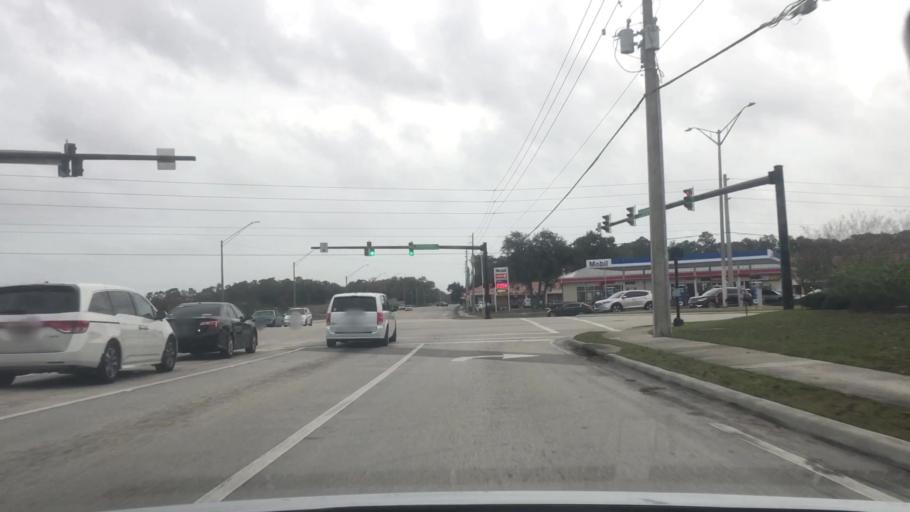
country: US
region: Florida
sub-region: Duval County
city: Atlantic Beach
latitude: 30.3483
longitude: -81.5237
